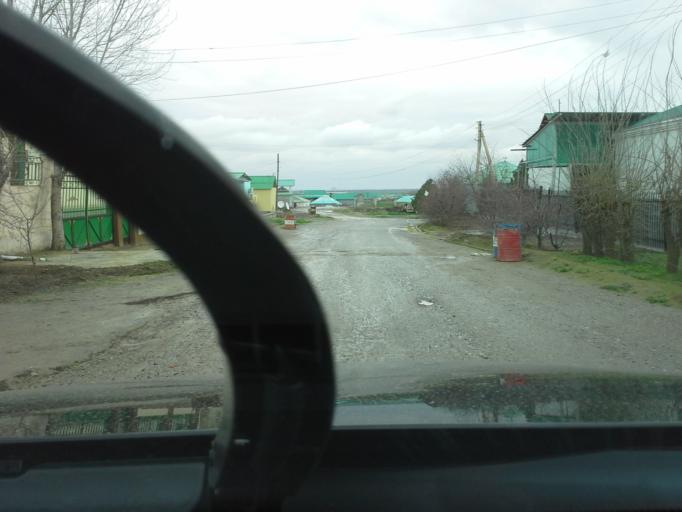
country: TM
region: Ahal
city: Abadan
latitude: 37.9648
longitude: 58.2041
